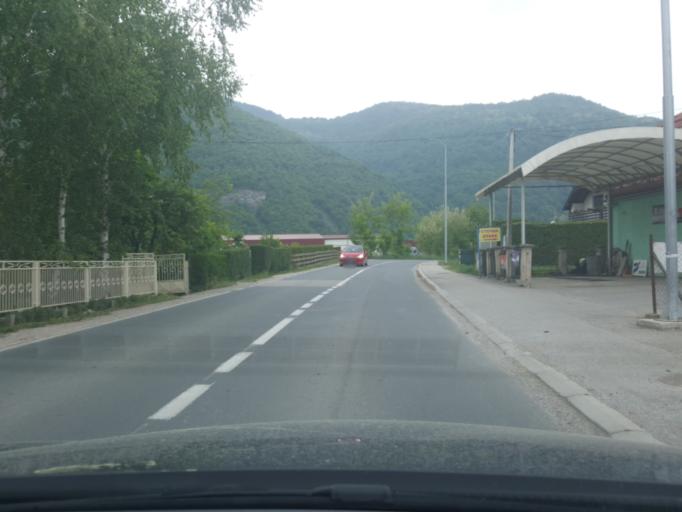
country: RS
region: Central Serbia
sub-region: Zlatiborski Okrug
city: Bajina Basta
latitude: 43.9950
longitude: 19.5658
